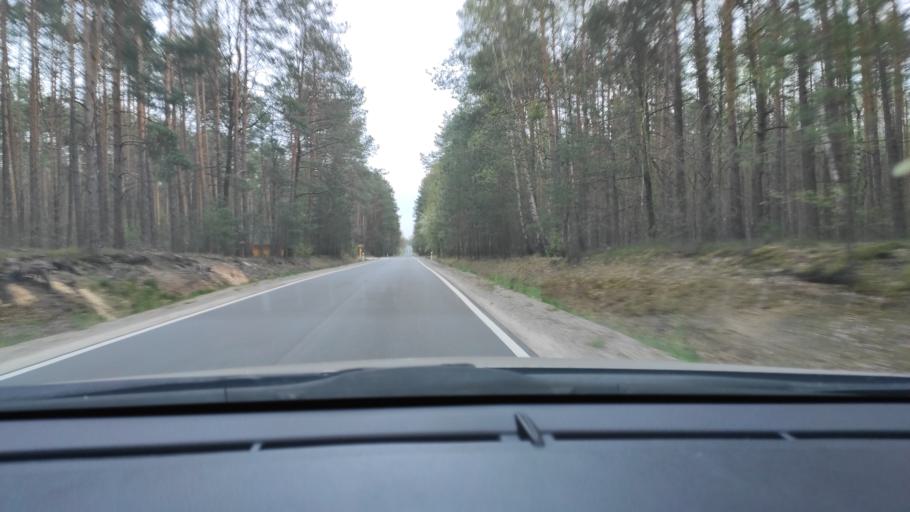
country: PL
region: Masovian Voivodeship
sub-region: Powiat zwolenski
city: Zwolen
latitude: 51.3907
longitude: 21.5491
